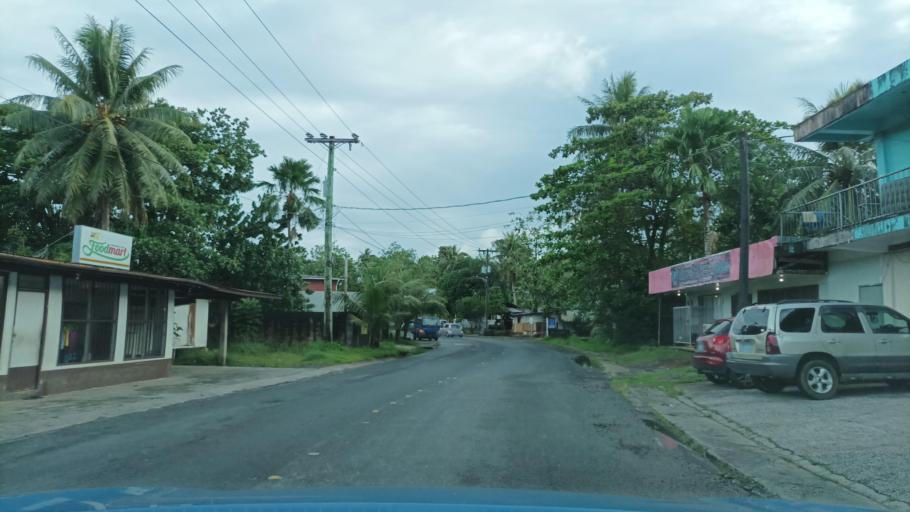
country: FM
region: Pohnpei
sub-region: Kolonia Municipality
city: Kolonia
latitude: 6.9642
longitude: 158.2148
